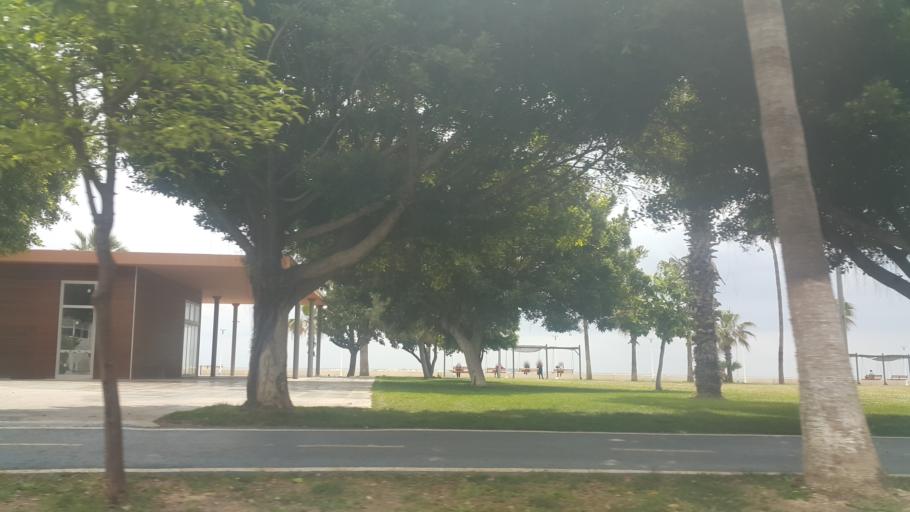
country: TR
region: Mersin
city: Mercin
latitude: 36.7667
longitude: 34.5584
